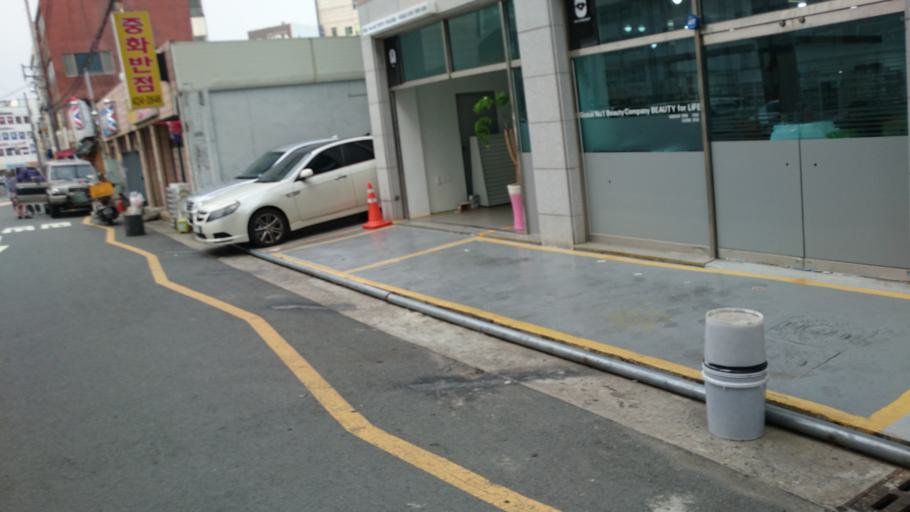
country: KR
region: Daegu
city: Daegu
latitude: 35.8628
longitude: 128.5984
